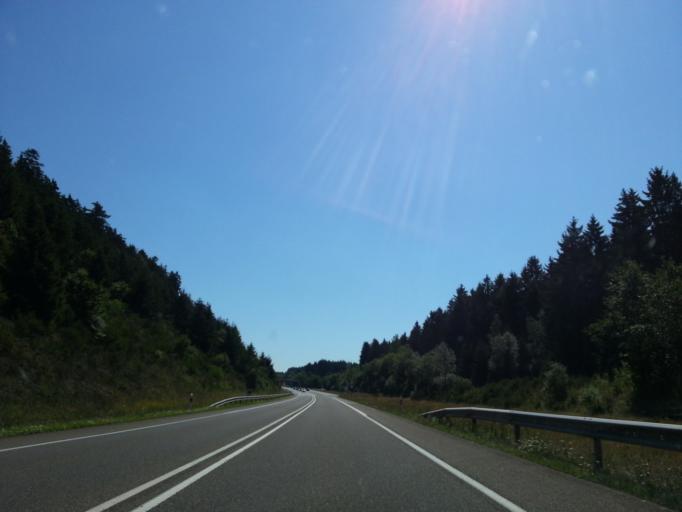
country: DE
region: Rheinland-Pfalz
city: Brandscheid
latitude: 50.2050
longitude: 6.3319
